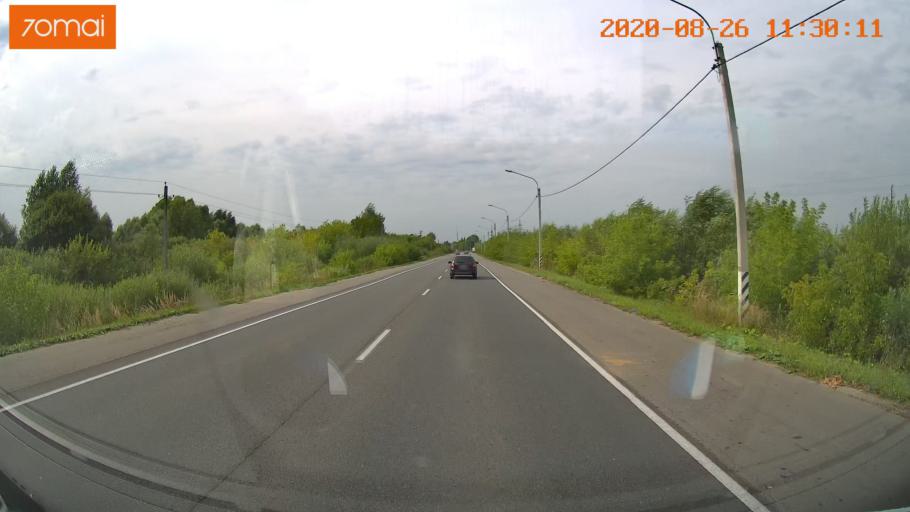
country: RU
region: Rjazan
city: Shilovo
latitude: 54.3164
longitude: 40.8879
